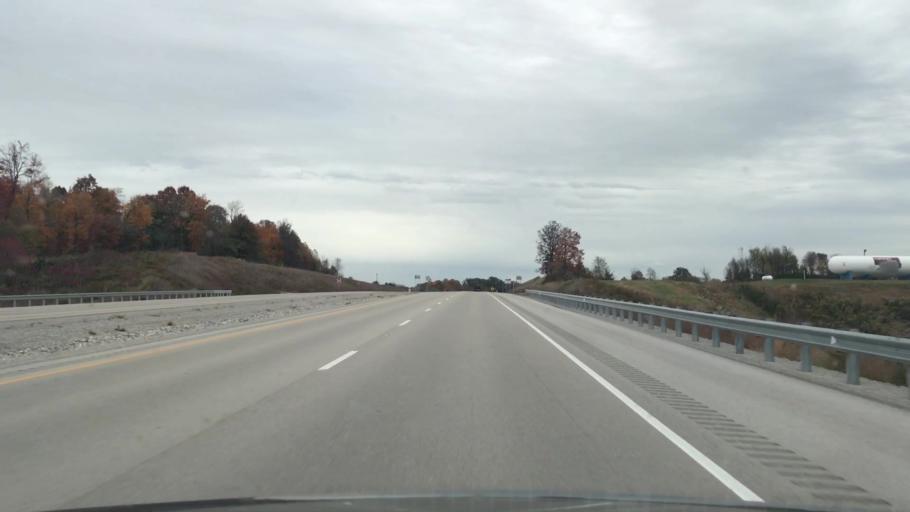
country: US
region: Kentucky
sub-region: Barren County
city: Glasgow
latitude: 37.0075
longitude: -85.9568
